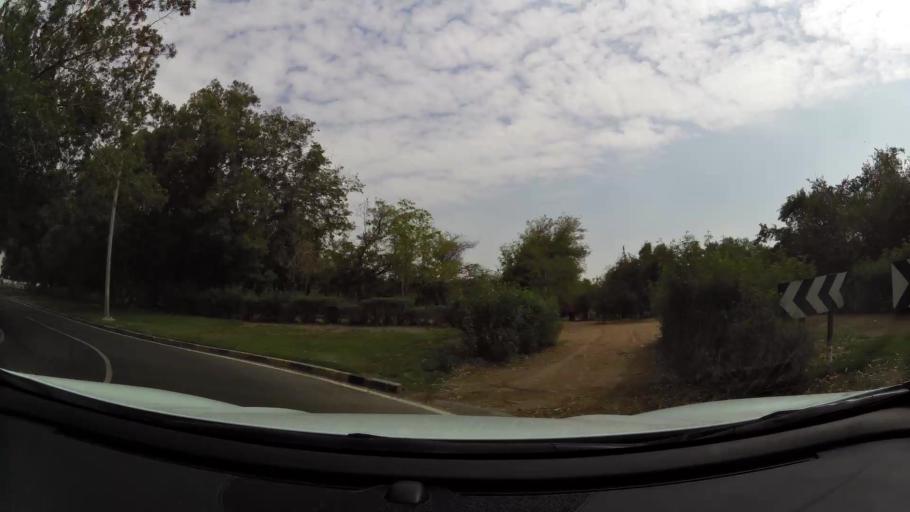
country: OM
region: Al Buraimi
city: Al Buraymi
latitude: 24.2068
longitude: 55.8056
